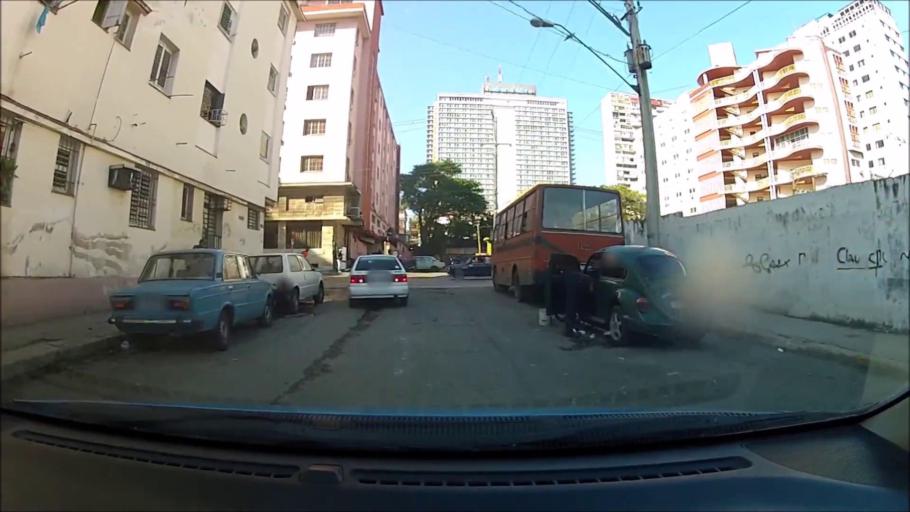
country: CU
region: La Habana
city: Havana
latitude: 23.1410
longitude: -82.3797
